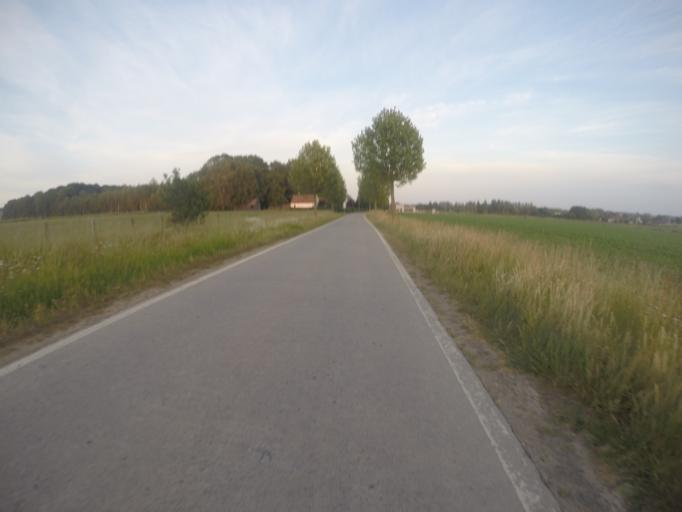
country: BE
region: Flanders
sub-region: Provincie Oost-Vlaanderen
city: Zomergem
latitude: 51.1215
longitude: 3.5334
